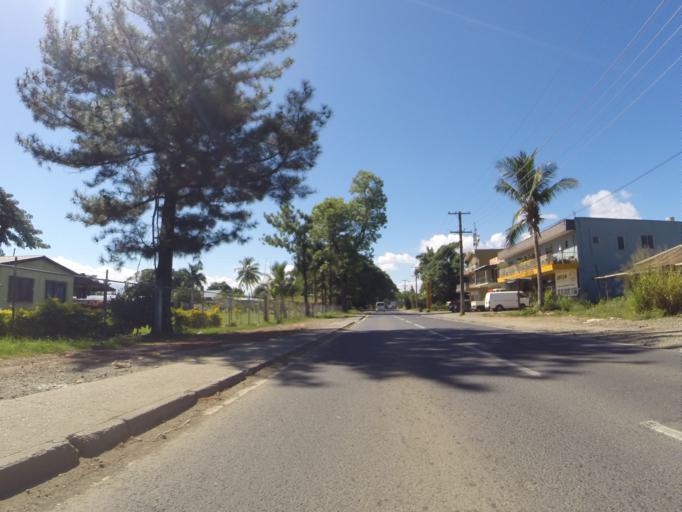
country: FJ
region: Western
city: Nadi
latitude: -17.7979
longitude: 177.4130
